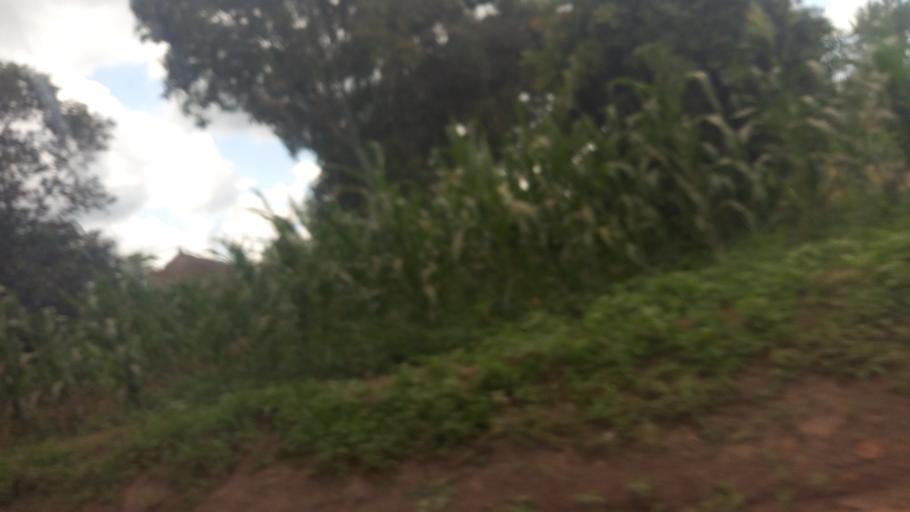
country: UG
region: Western Region
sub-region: Kiryandongo District
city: Kiryandongo
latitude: 1.9305
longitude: 32.1320
